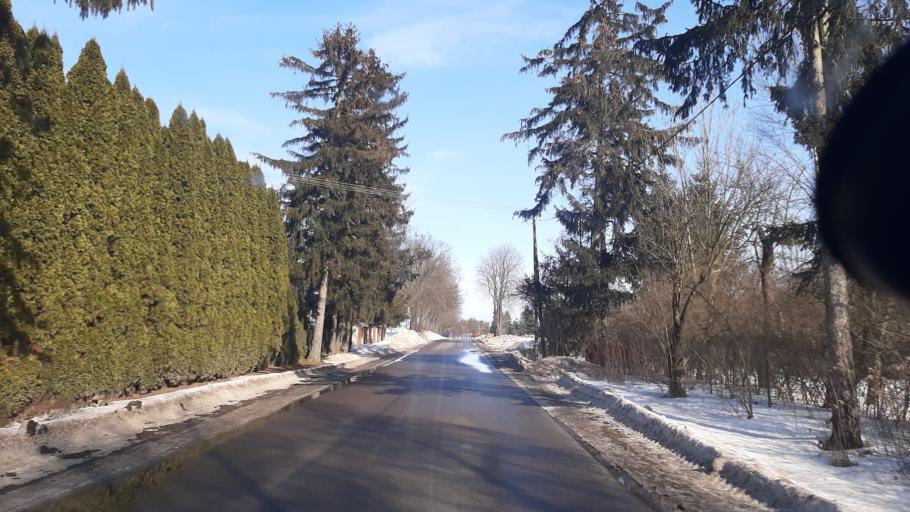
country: PL
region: Lublin Voivodeship
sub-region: Powiat pulawski
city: Kurow
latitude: 51.3763
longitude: 22.1545
